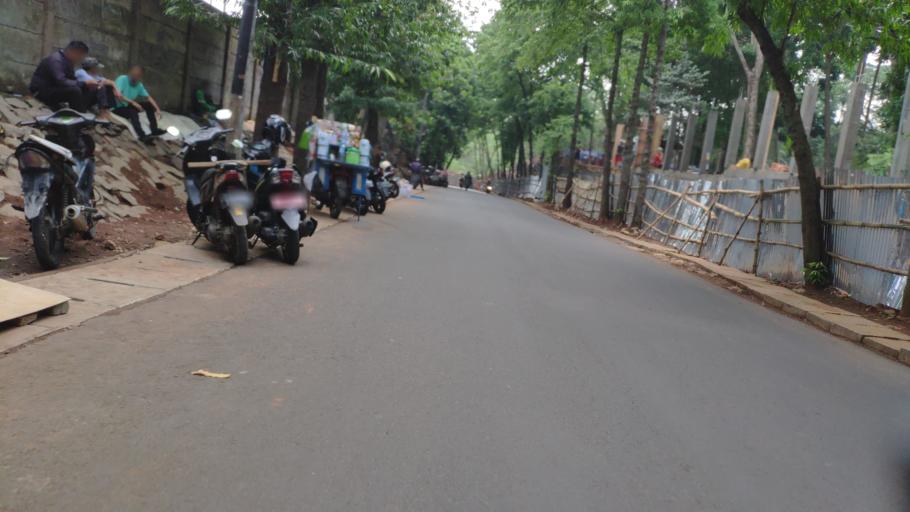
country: ID
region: West Java
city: Pamulang
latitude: -6.3065
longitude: 106.8215
